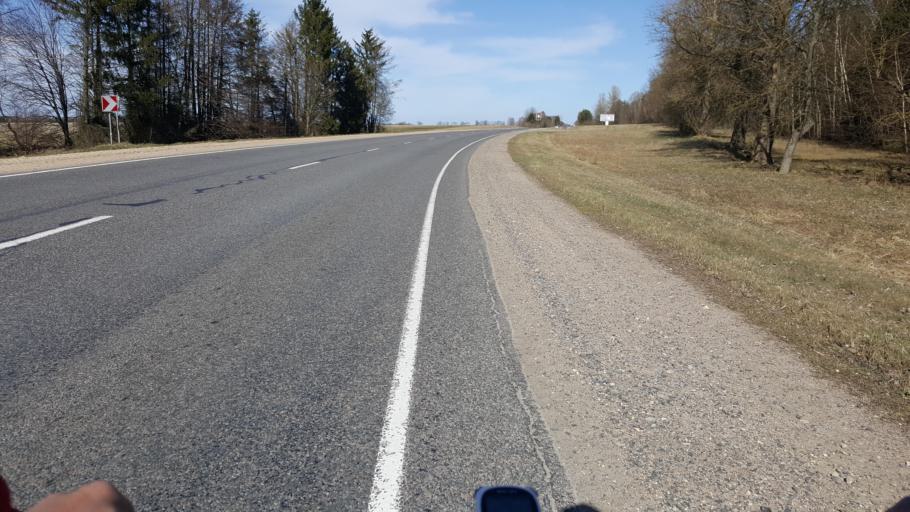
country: BY
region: Brest
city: Kamyanyets
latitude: 52.3588
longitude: 23.7769
